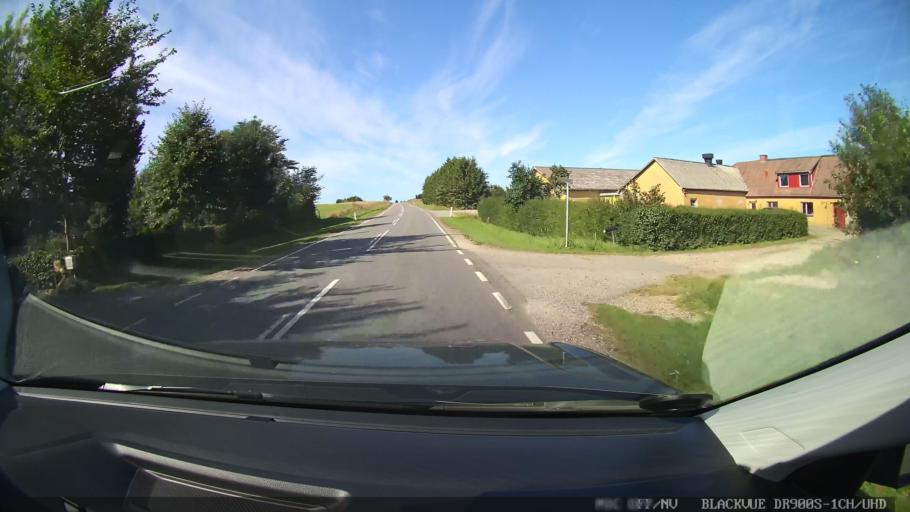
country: DK
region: North Denmark
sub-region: Mariagerfjord Kommune
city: Mariager
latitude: 56.6901
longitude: 9.9531
